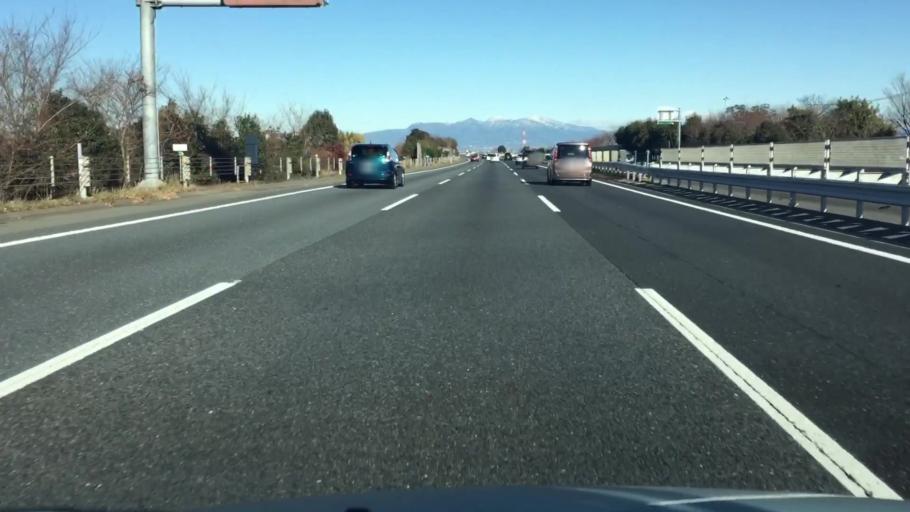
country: JP
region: Saitama
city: Honjo
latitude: 36.1832
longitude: 139.1907
